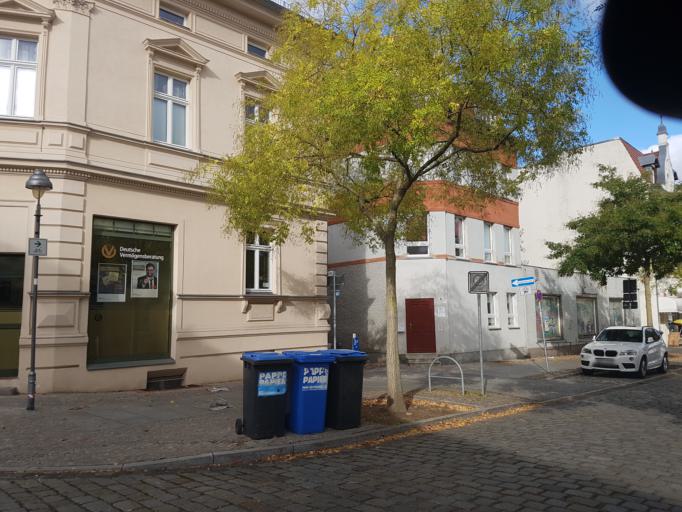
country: DE
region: Brandenburg
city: Nauen
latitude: 52.6081
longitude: 12.8784
